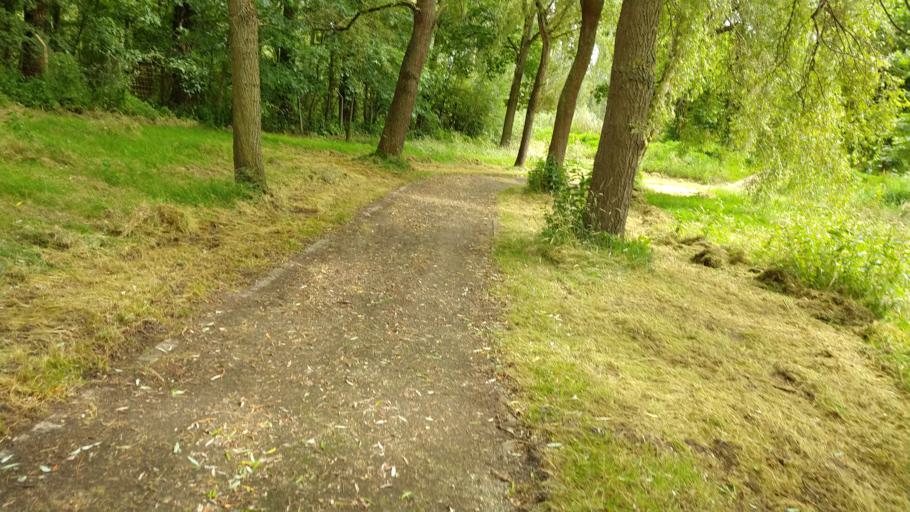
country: BE
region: Flanders
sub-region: Provincie Vlaams-Brabant
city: Diest
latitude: 50.9822
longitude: 5.0671
